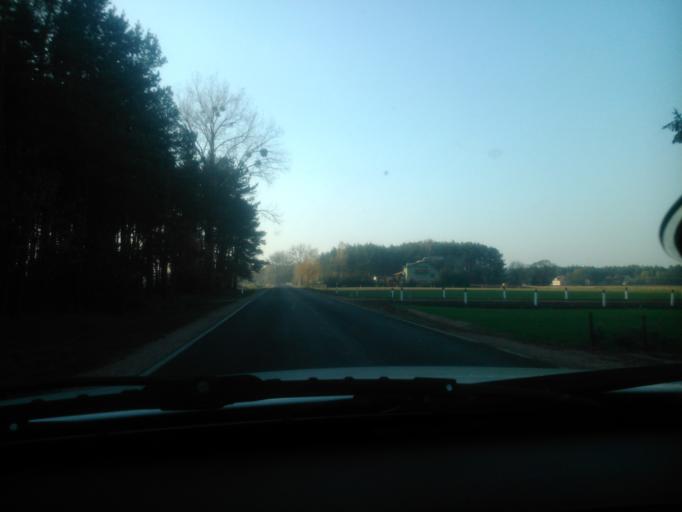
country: PL
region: Masovian Voivodeship
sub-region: Powiat ostrolecki
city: Czarnia
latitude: 53.2982
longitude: 21.0911
